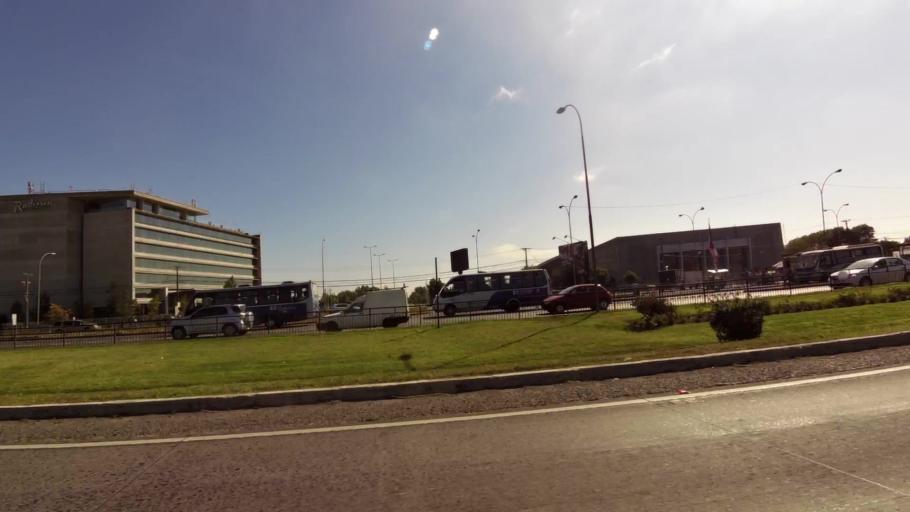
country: CL
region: Biobio
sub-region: Provincia de Concepcion
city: Concepcion
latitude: -36.7921
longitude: -73.0699
